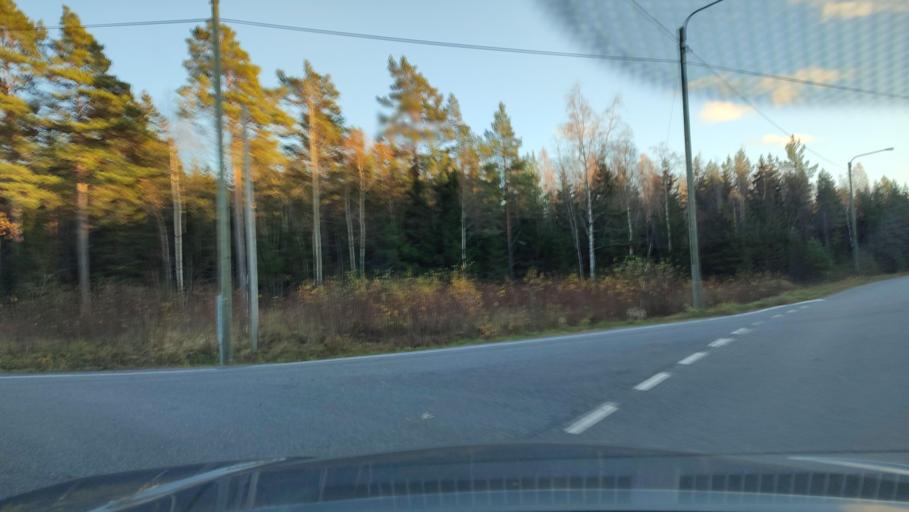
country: FI
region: Ostrobothnia
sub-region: Sydosterbotten
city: Kristinestad
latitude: 62.2627
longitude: 21.3490
